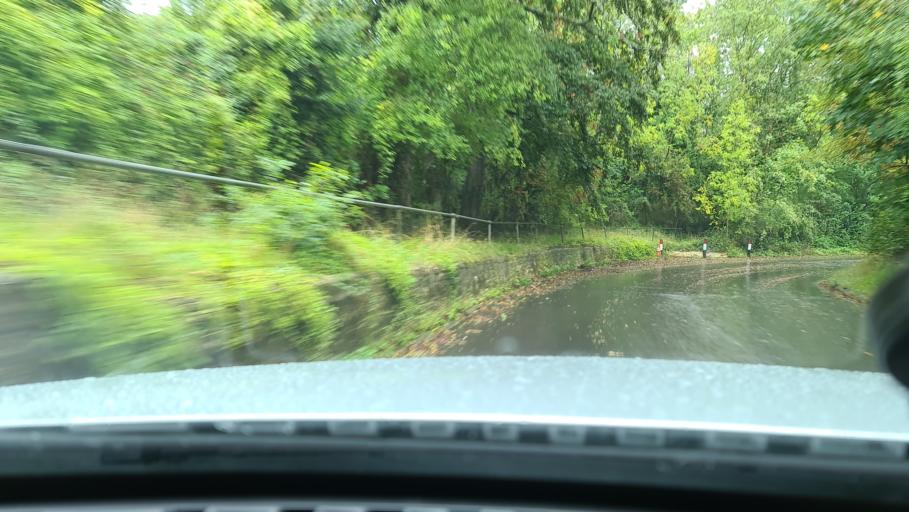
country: GB
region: England
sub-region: Oxfordshire
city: Somerton
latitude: 51.9220
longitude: -1.3059
